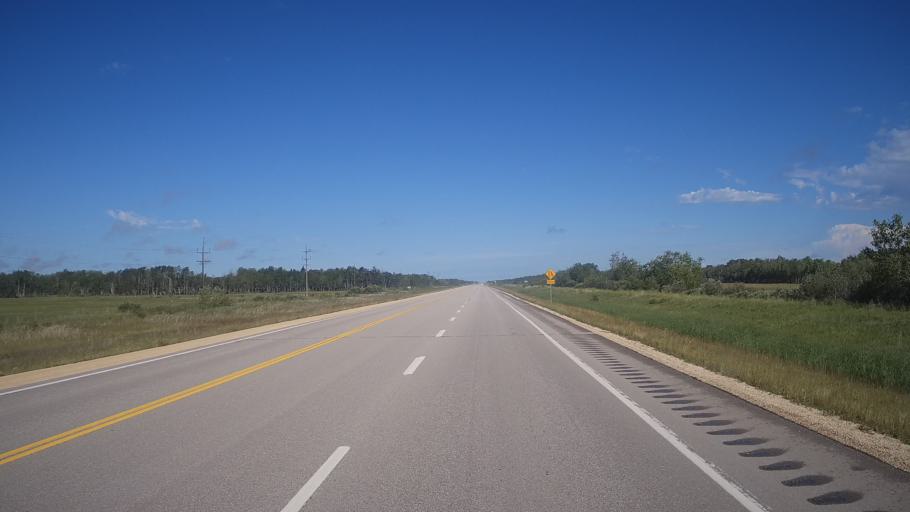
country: CA
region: Manitoba
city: Stonewall
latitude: 50.2297
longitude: -97.6971
